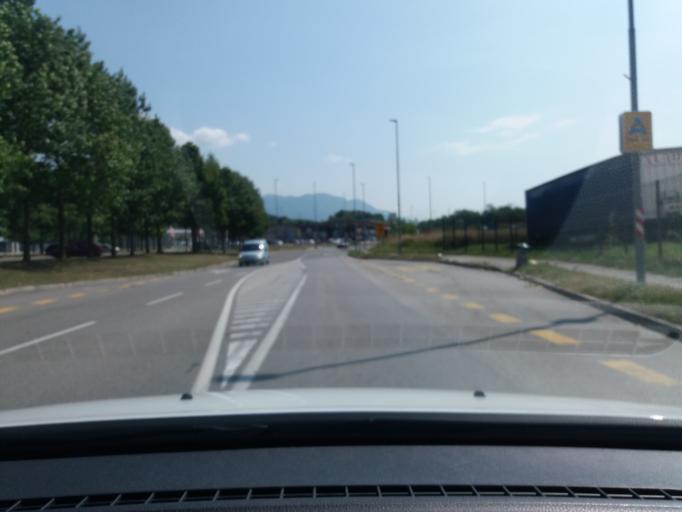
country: SI
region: Sempeter-Vrtojba
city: Sempeter pri Gorici
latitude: 45.9216
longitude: 13.6384
